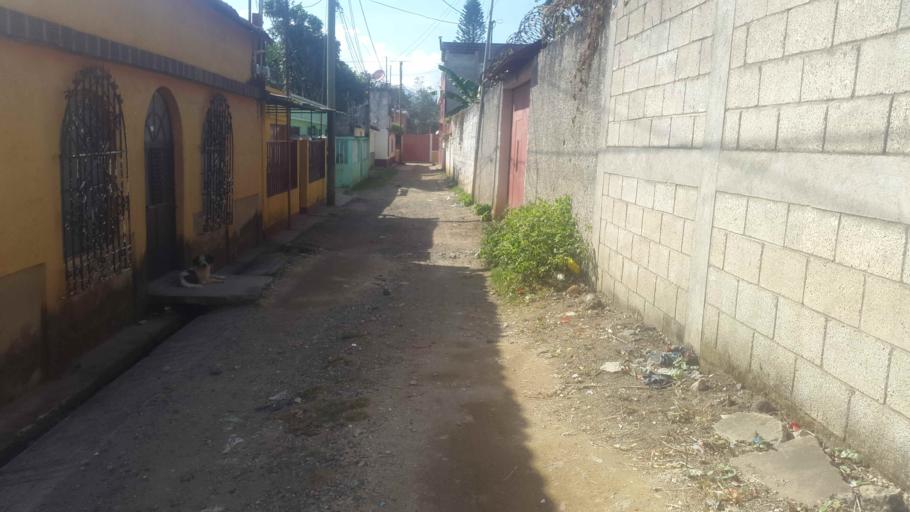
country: GT
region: Guatemala
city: Petapa
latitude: 14.5137
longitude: -90.5422
